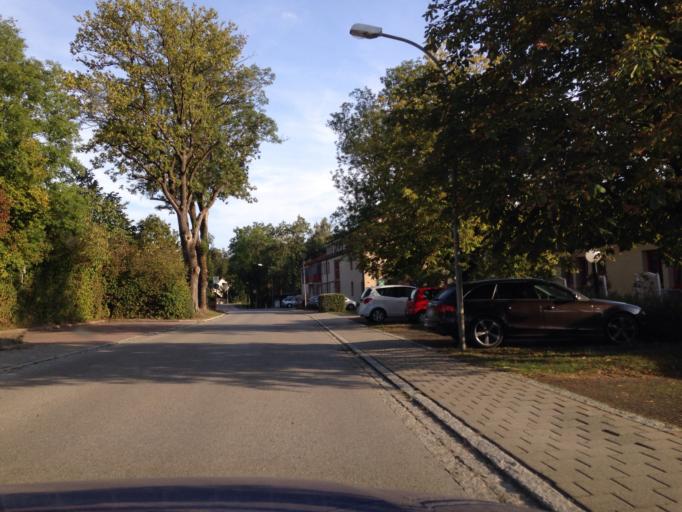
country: DE
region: Bavaria
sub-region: Regierungsbezirk Mittelfranken
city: Thalmassing
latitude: 49.0916
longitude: 11.2213
